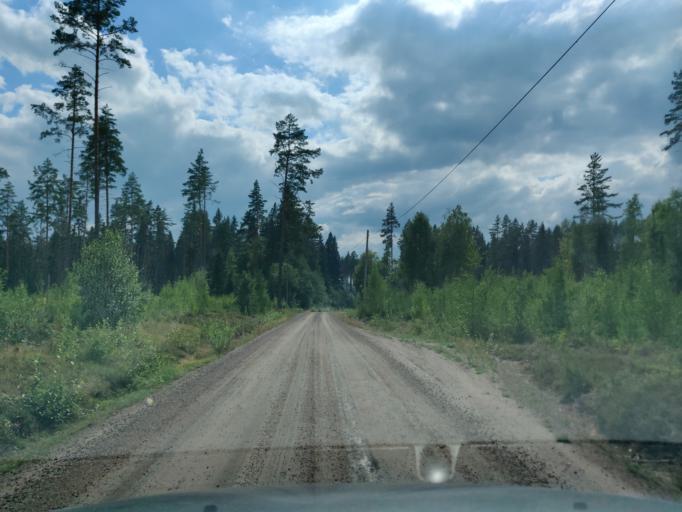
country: SE
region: Vaermland
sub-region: Hagfors Kommun
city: Hagfors
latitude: 59.9882
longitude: 13.5633
